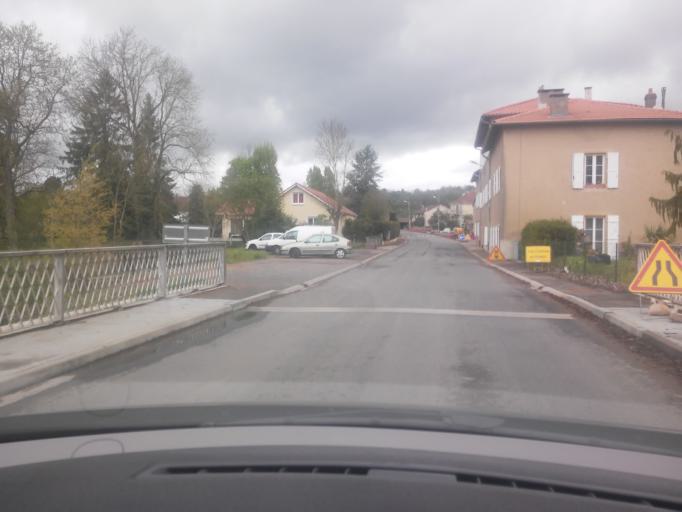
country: FR
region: Lorraine
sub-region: Departement de la Moselle
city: Courcelles-Chaussy
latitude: 49.0837
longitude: 6.3631
